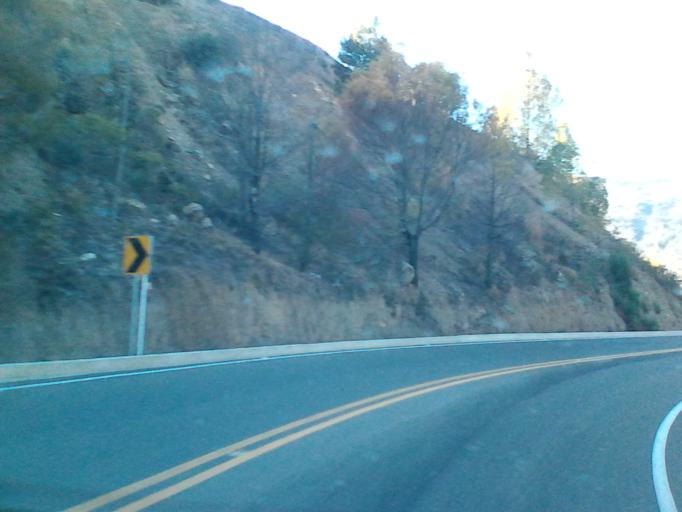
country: CO
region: Boyaca
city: Cucaita
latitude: 5.5470
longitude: -73.4455
